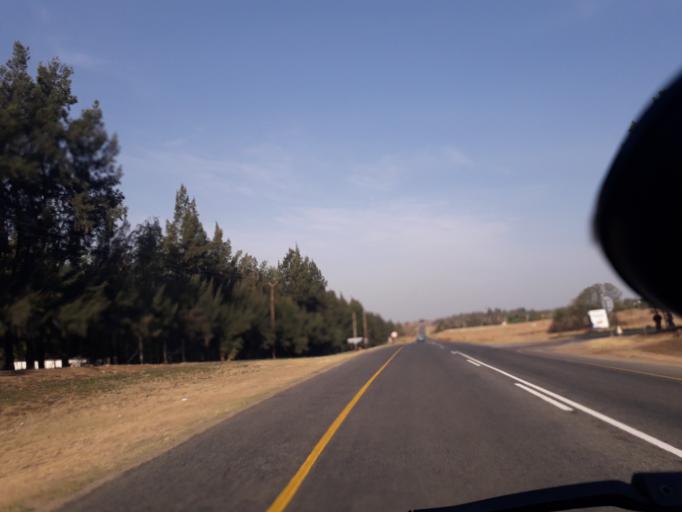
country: ZA
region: Gauteng
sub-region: West Rand District Municipality
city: Muldersdriseloop
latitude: -25.9601
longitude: 27.8871
